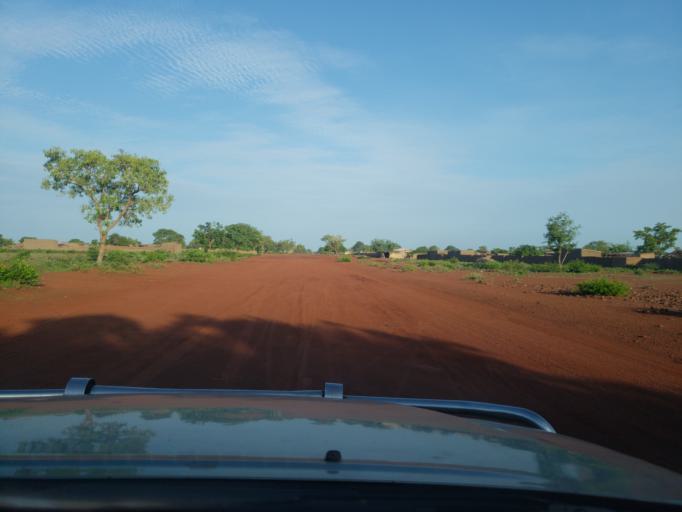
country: ML
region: Sikasso
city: Koutiala
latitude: 12.4044
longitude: -5.5279
